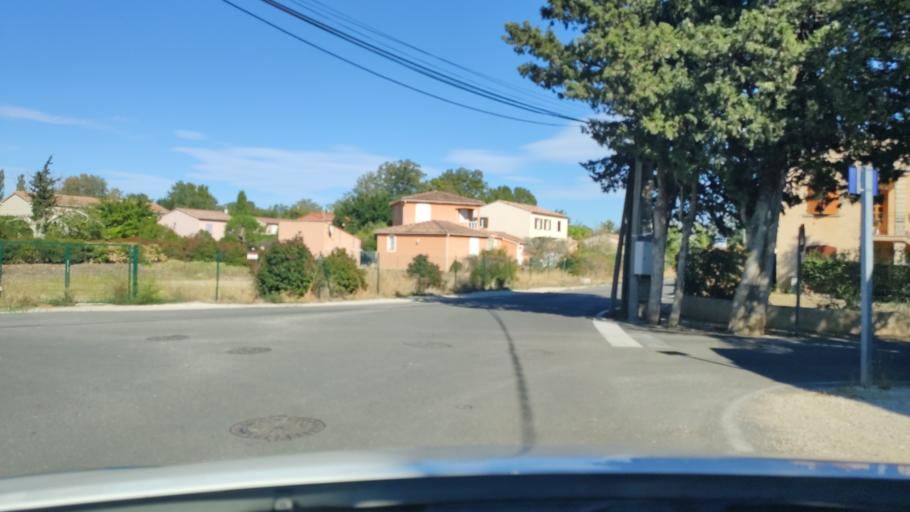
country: FR
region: Provence-Alpes-Cote d'Azur
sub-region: Departement du Vaucluse
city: Montfavet
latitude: 43.9279
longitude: 4.8868
